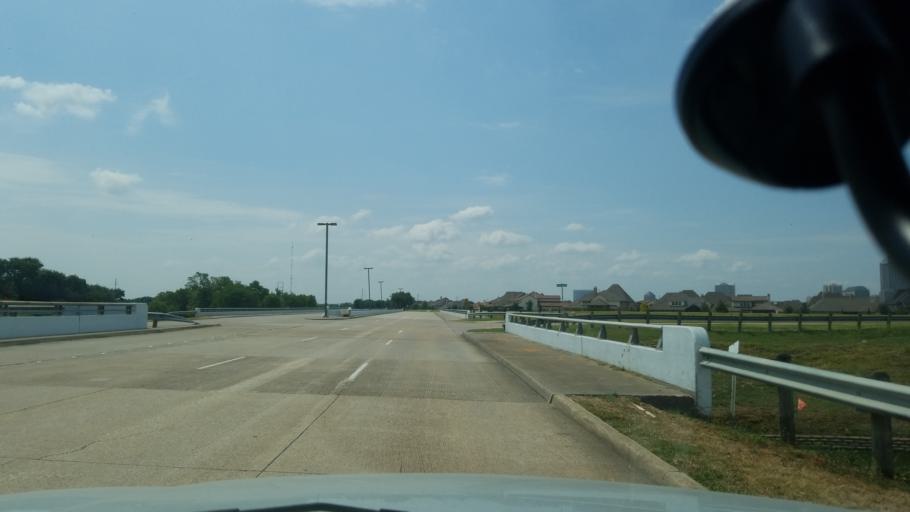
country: US
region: Texas
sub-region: Dallas County
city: Farmers Branch
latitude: 32.8861
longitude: -96.9343
